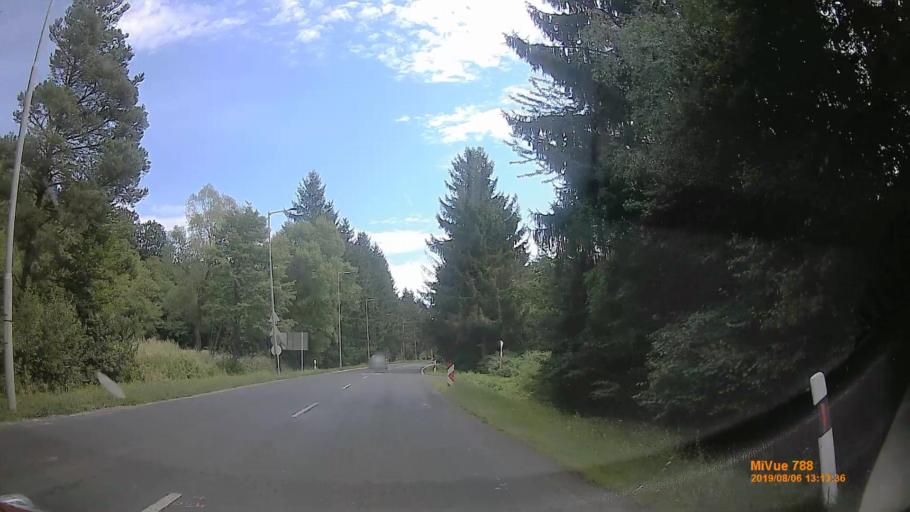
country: AT
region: Burgenland
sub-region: Politischer Bezirk Oberpullendorf
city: Mannersdorf an der Rabnitz
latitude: 47.4069
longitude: 16.5248
